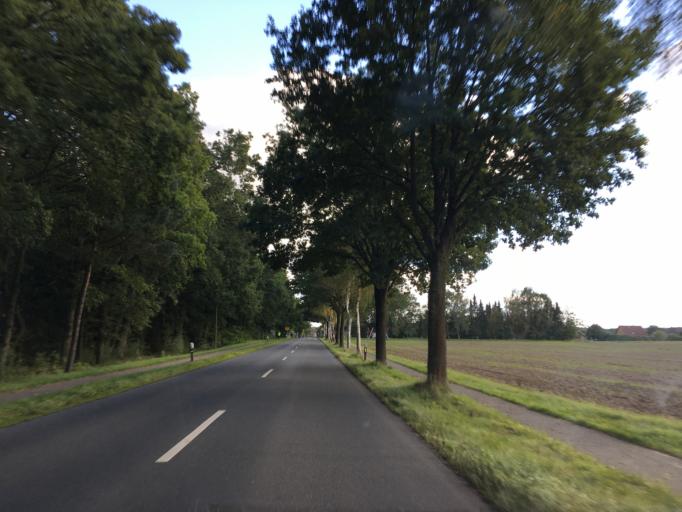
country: DE
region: Lower Saxony
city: Westergellersen
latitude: 53.2412
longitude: 10.2375
